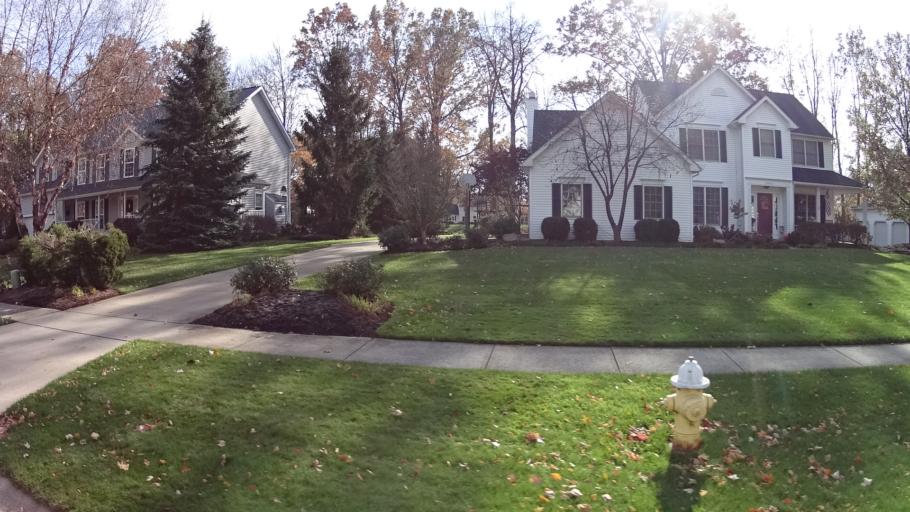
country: US
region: Ohio
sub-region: Lorain County
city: Avon Lake
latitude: 41.4994
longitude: -82.0285
